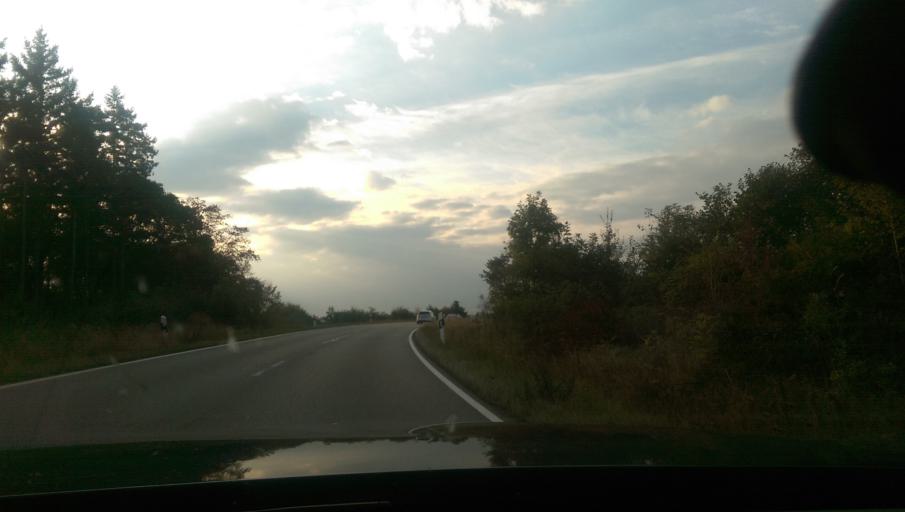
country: DE
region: Baden-Wuerttemberg
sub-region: Karlsruhe Region
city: Friolzheim
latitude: 48.8355
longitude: 8.8588
